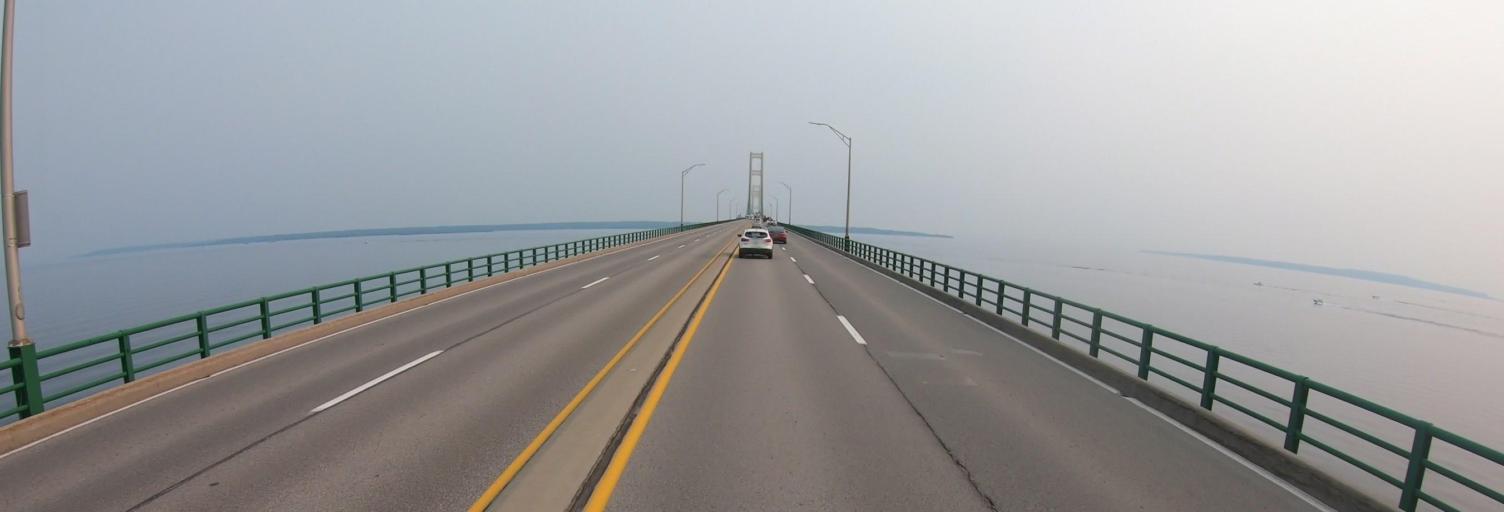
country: US
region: Michigan
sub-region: Mackinac County
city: Saint Ignace
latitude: 45.7975
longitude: -84.7297
